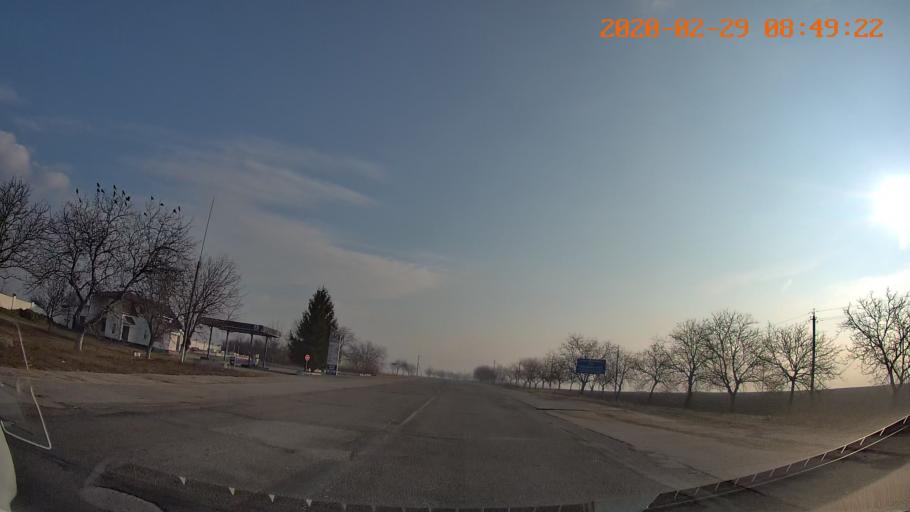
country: MD
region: Anenii Noi
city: Varnita
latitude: 46.9215
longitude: 29.4946
